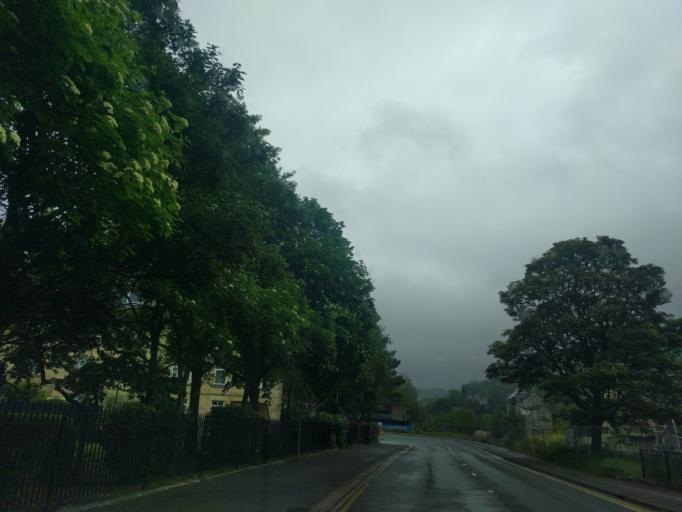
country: GB
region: England
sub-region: Bath and North East Somerset
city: Bath
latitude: 51.3795
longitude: -2.3654
